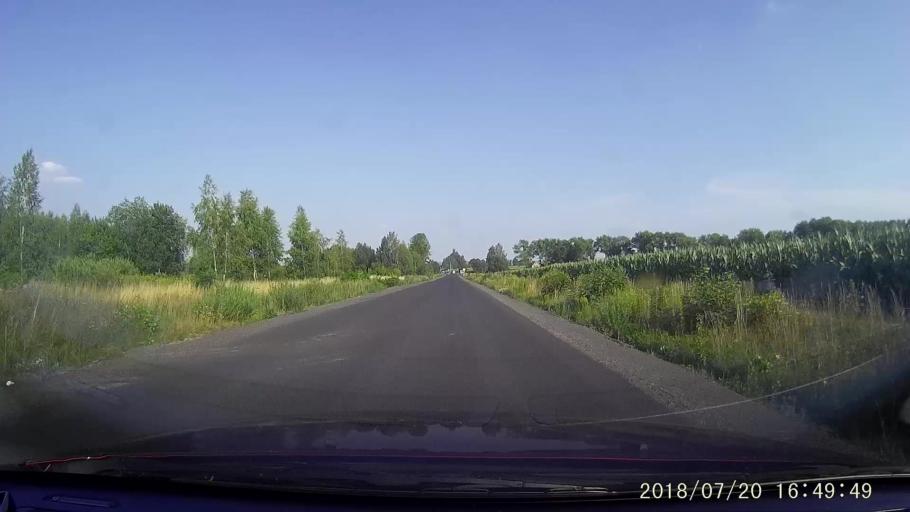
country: PL
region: Lower Silesian Voivodeship
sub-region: Powiat lubanski
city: Lesna
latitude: 51.0452
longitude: 15.2004
